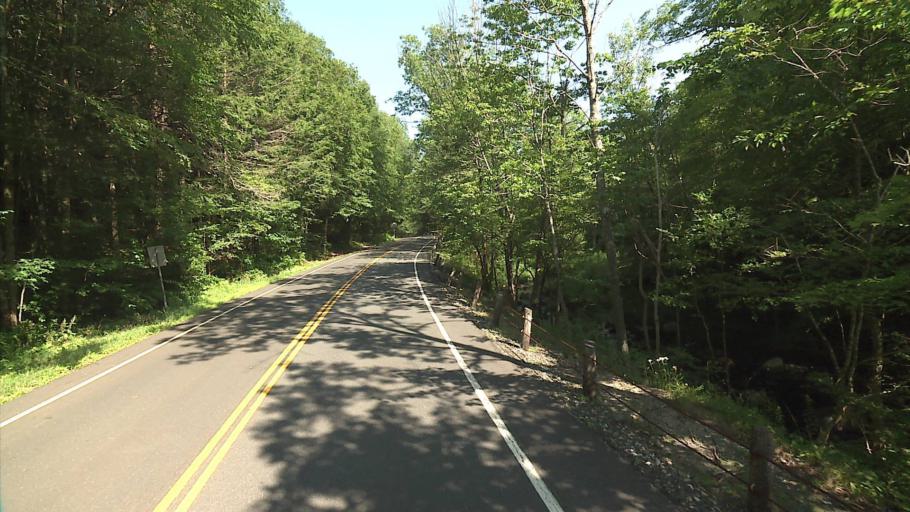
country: US
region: Massachusetts
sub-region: Berkshire County
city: New Marlborough
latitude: 42.0416
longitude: -73.1346
